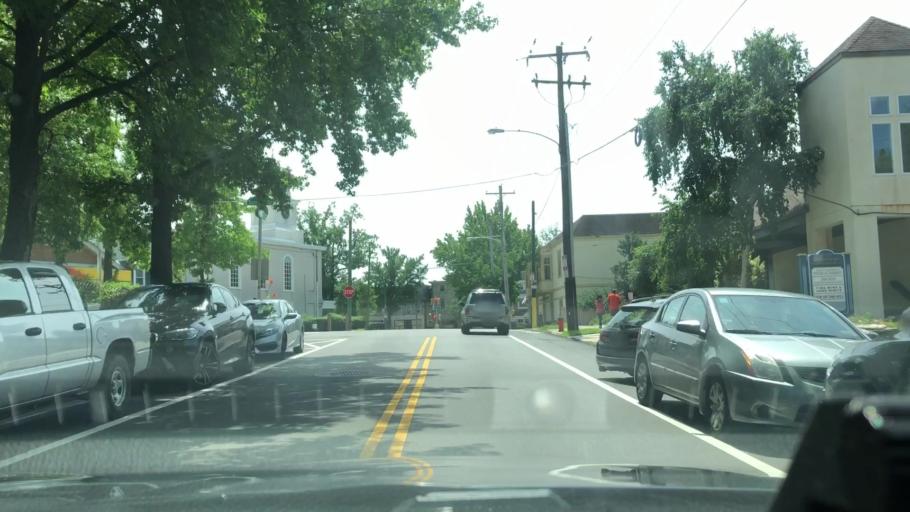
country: US
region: Pennsylvania
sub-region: Montgomery County
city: Wyndmoor
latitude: 40.0783
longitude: -75.2081
